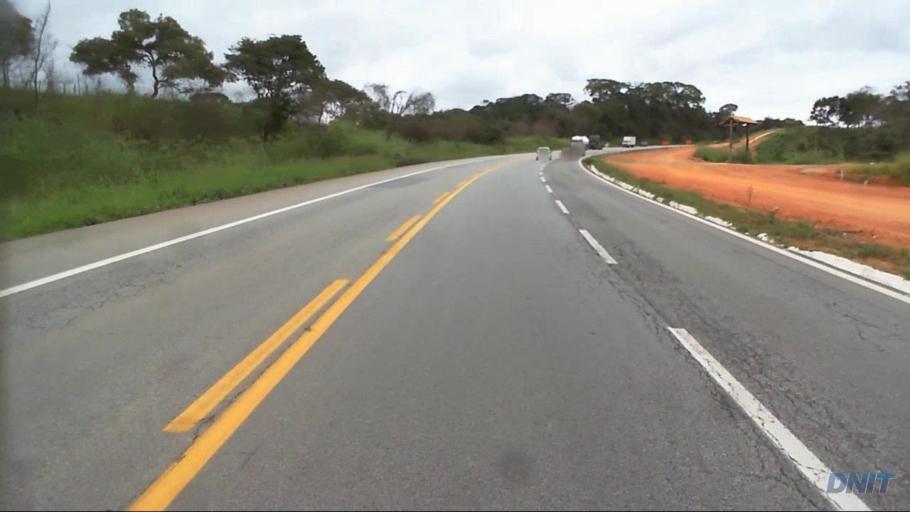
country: BR
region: Minas Gerais
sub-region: Barao De Cocais
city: Barao de Cocais
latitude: -19.7587
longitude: -43.4689
